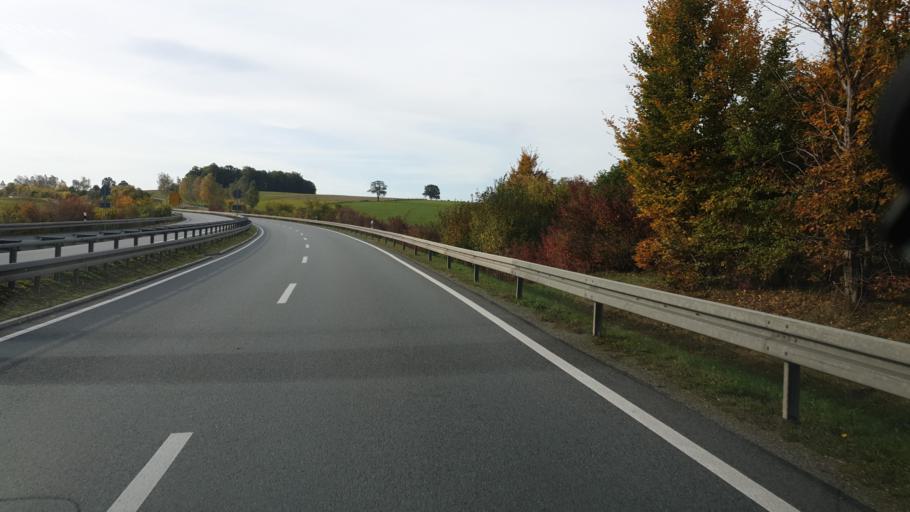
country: DE
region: Saxony
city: Lobau
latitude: 51.0976
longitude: 14.6406
